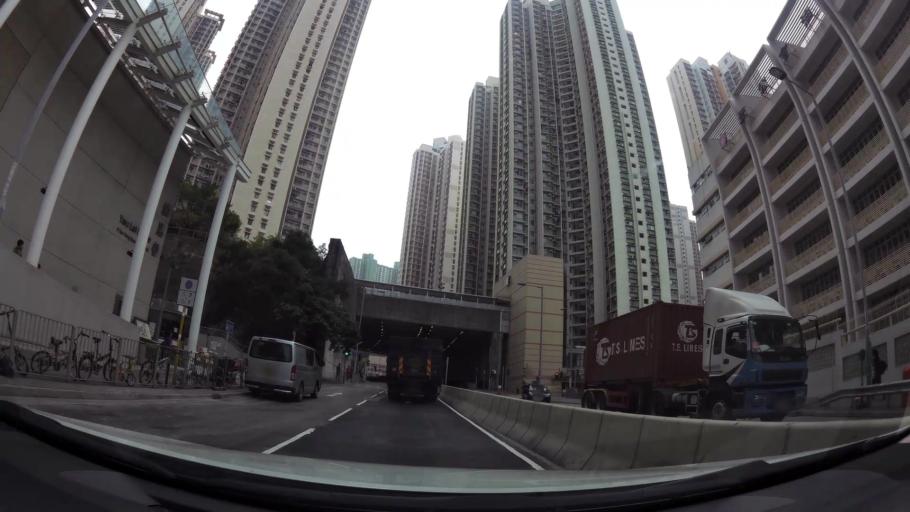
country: HK
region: Kowloon City
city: Kowloon
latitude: 22.3004
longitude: 114.2352
